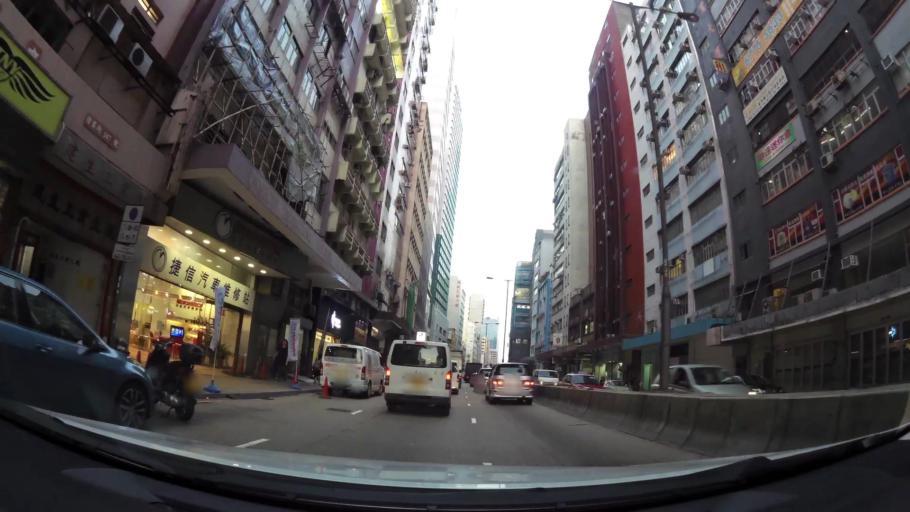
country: HK
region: Kowloon City
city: Kowloon
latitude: 22.3130
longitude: 114.2183
